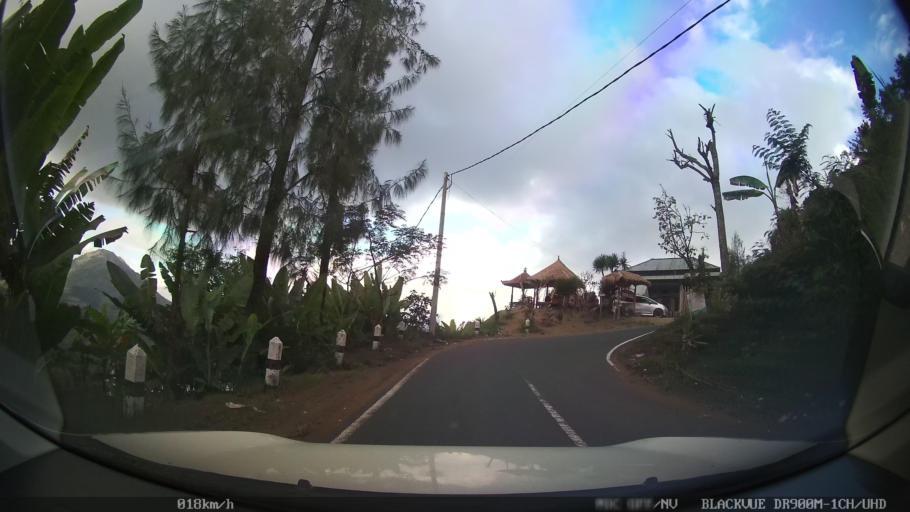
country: ID
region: Bali
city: Banjar Kedisan
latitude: -8.2597
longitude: 115.3408
